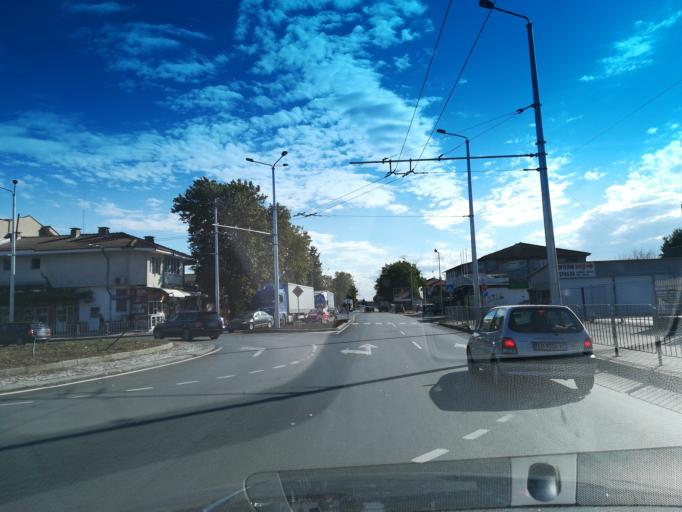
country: BG
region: Stara Zagora
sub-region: Obshtina Stara Zagora
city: Stara Zagora
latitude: 42.3988
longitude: 25.6443
